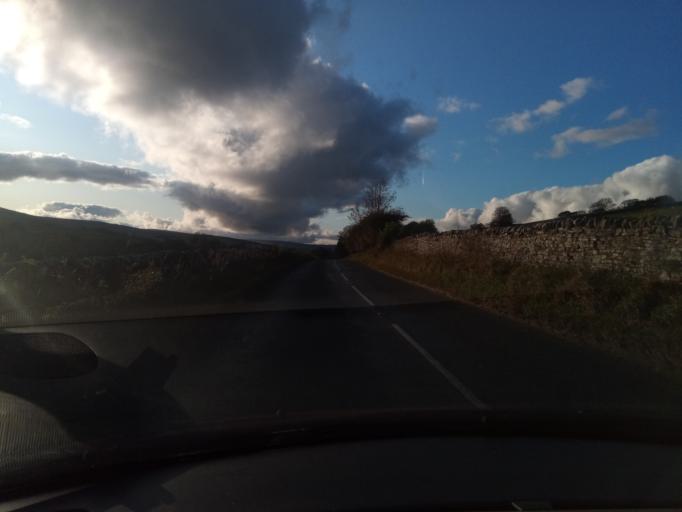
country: GB
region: England
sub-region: County Durham
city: Newbiggin
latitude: 54.7375
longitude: -2.1255
